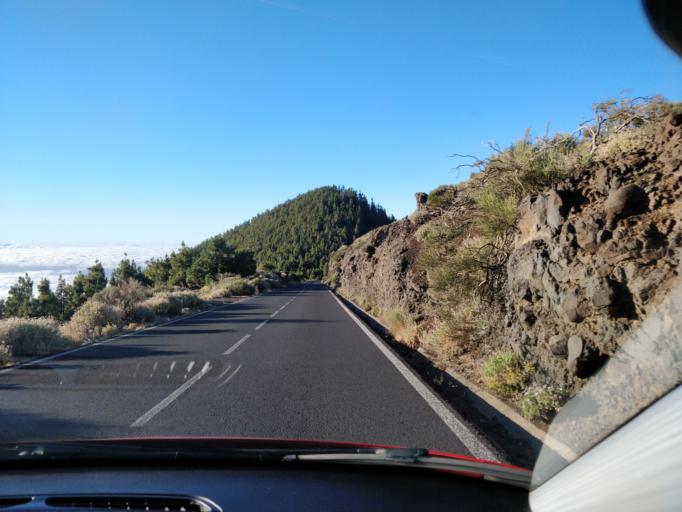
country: ES
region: Canary Islands
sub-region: Provincia de Santa Cruz de Tenerife
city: Arafo
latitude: 28.3419
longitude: -16.4827
